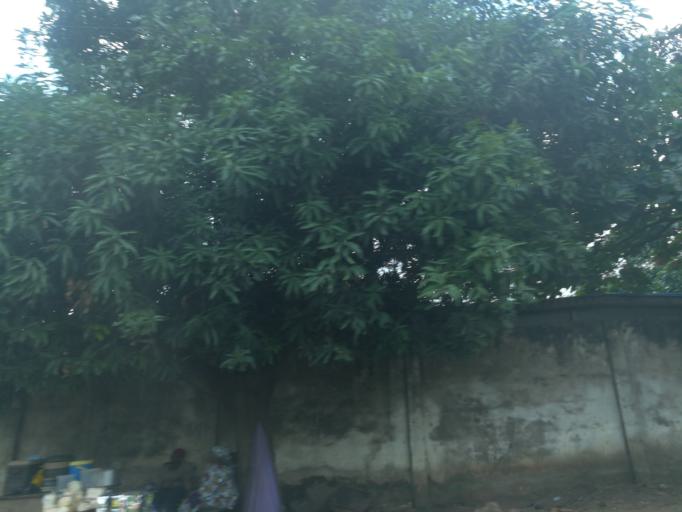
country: NG
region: Lagos
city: Ojota
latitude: 6.6055
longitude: 3.3670
